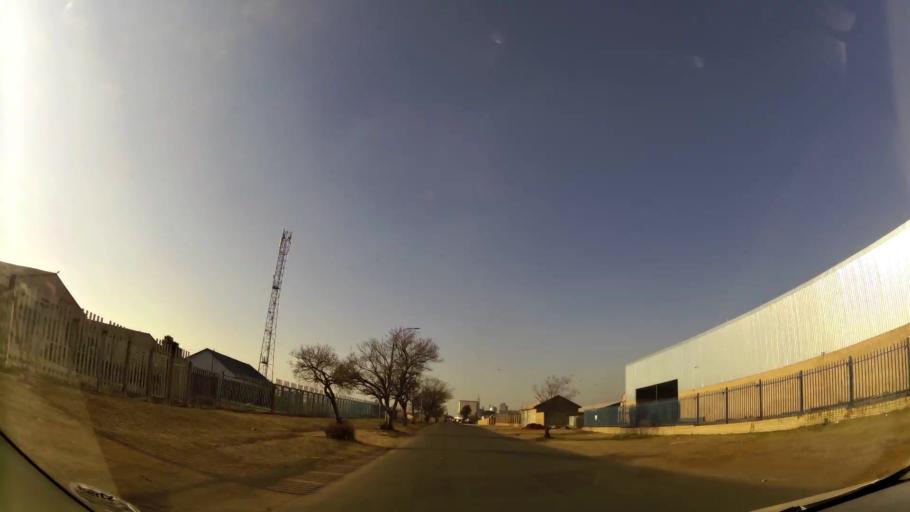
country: ZA
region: Gauteng
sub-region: West Rand District Municipality
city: Randfontein
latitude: -26.1957
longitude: 27.6845
